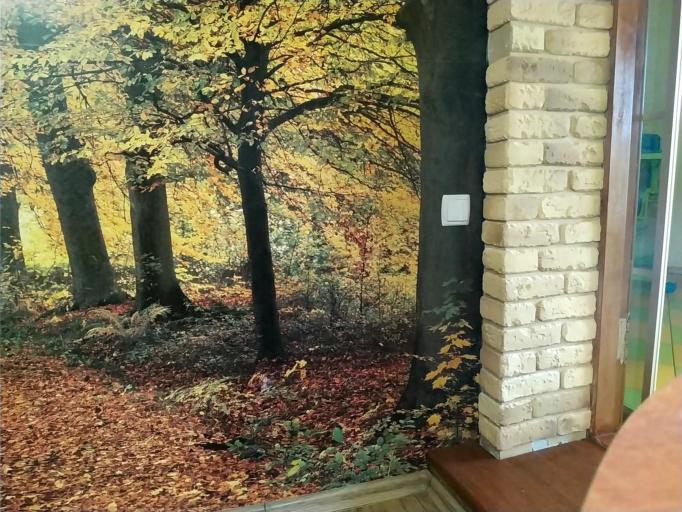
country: RU
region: Smolensk
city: Dorogobuzh
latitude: 54.8272
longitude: 33.3415
